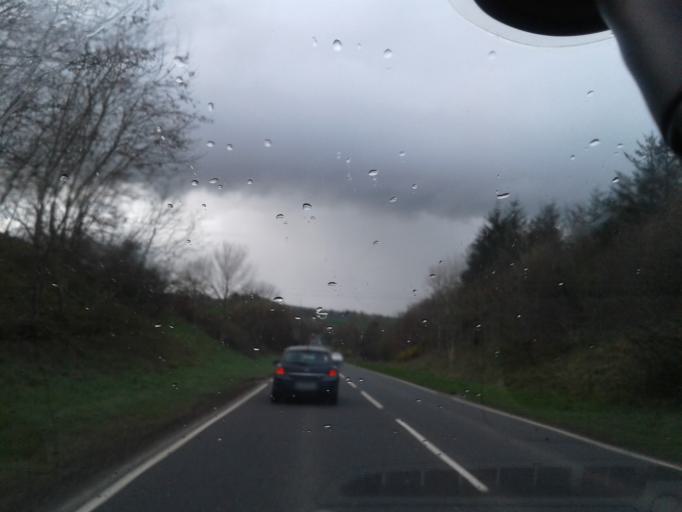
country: GB
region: Northern Ireland
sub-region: Strabane District
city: Sion Mills
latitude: 54.7613
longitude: -7.4587
